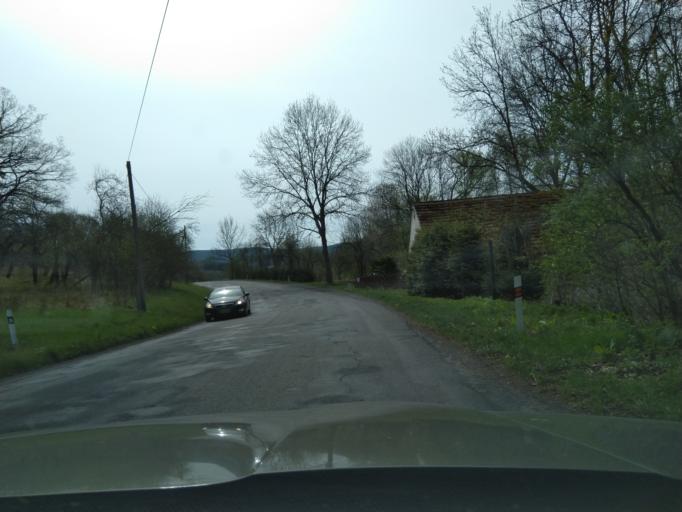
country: CZ
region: Plzensky
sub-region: Okres Klatovy
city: Kasperske Hory
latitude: 49.1881
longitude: 13.6251
